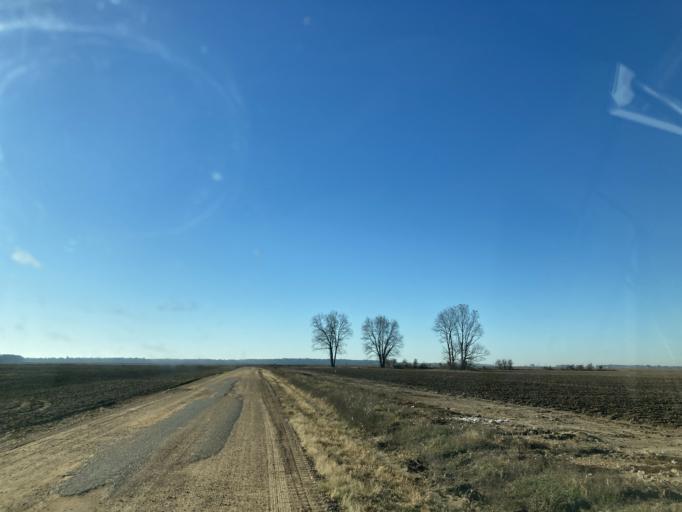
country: US
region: Mississippi
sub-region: Yazoo County
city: Yazoo City
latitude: 32.9211
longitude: -90.5942
